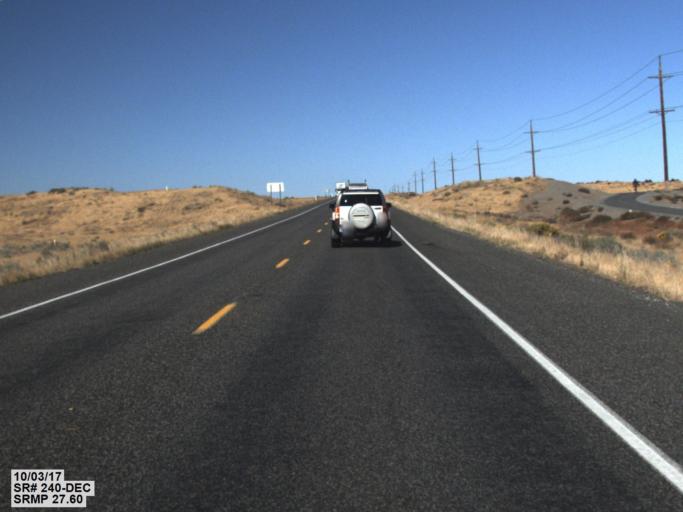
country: US
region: Washington
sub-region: Benton County
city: Richland
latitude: 46.3199
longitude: -119.3052
